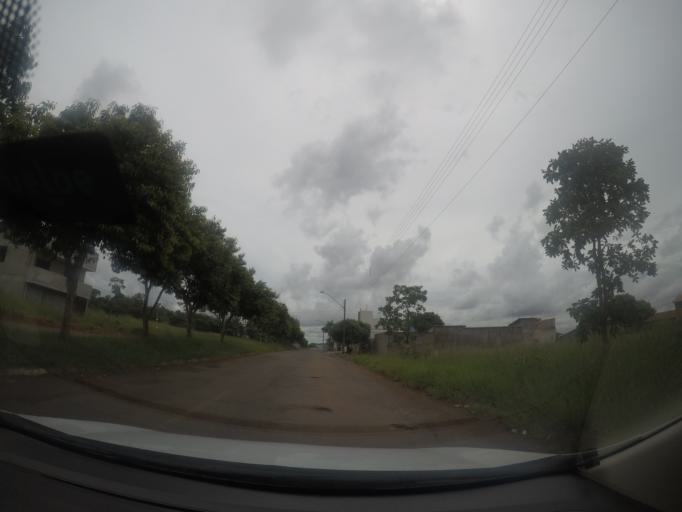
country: BR
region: Goias
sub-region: Trindade
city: Trindade
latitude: -16.6895
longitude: -49.3875
